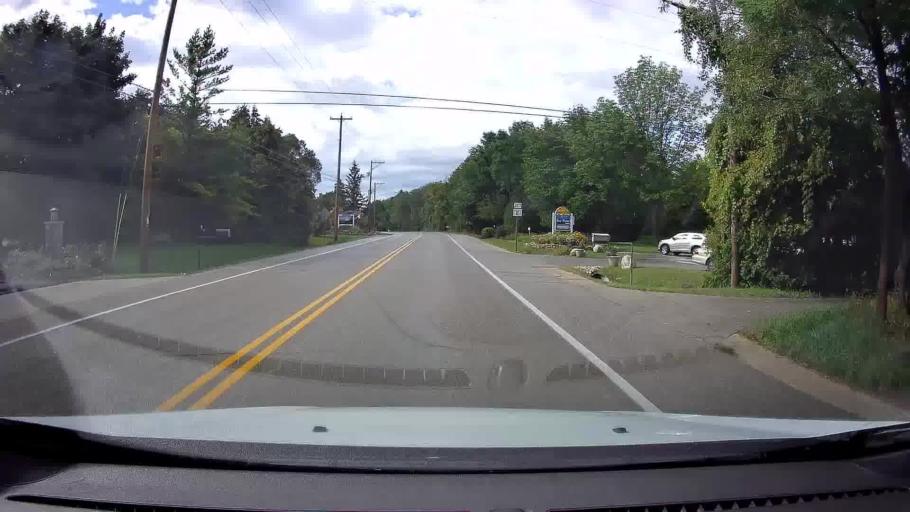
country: US
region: Wisconsin
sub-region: Door County
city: Sturgeon Bay
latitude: 45.0569
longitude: -87.2795
